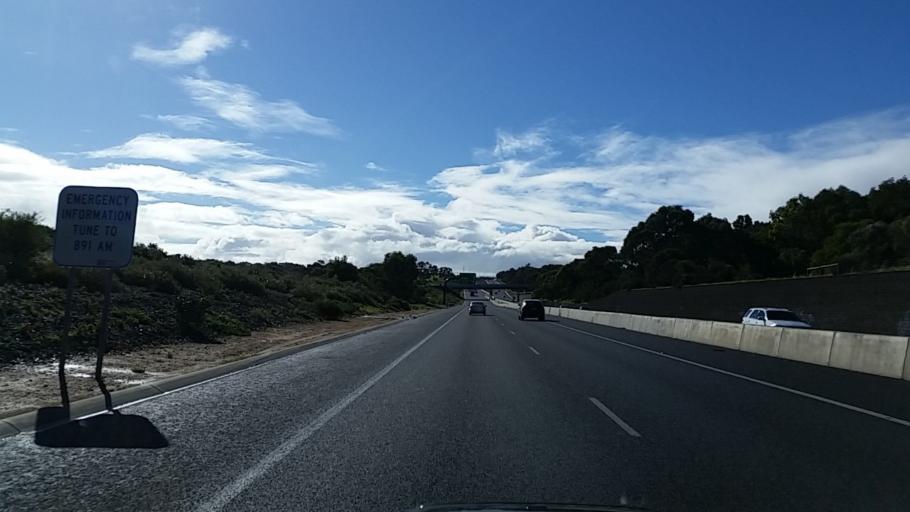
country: AU
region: South Australia
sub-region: Onkaparinga
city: Noarlunga Downs
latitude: -35.1520
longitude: 138.5057
